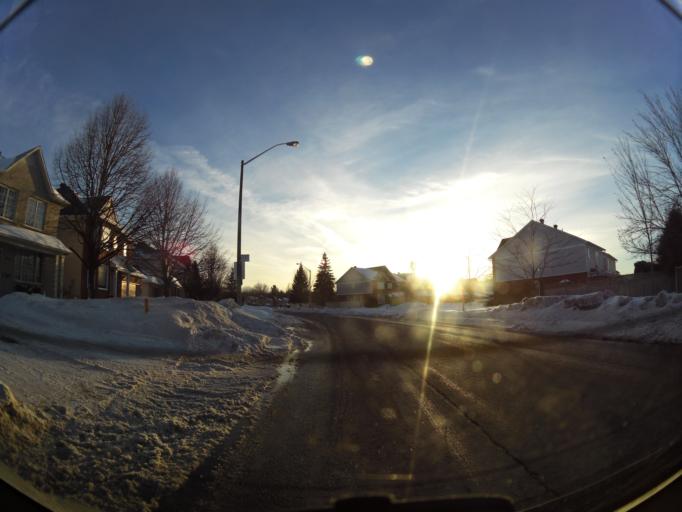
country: CA
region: Ontario
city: Ottawa
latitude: 45.4415
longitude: -75.5309
